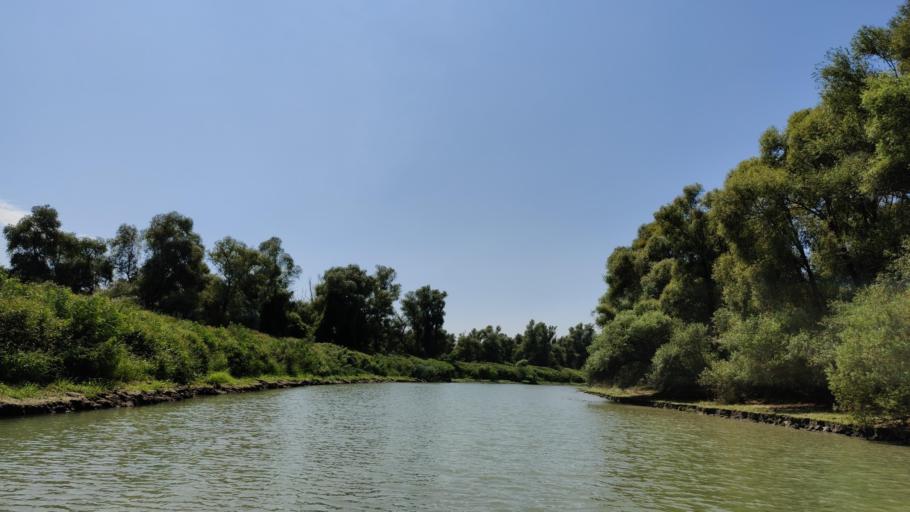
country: RO
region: Tulcea
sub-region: Comuna Pardina
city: Pardina
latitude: 45.2552
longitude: 28.9560
